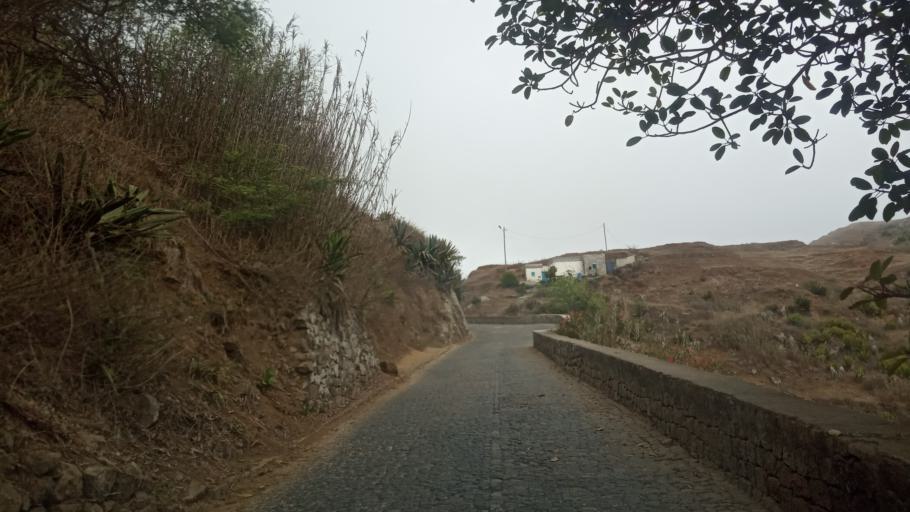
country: CV
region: Brava
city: Vila Nova Sintra
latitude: 14.8716
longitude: -24.7004
